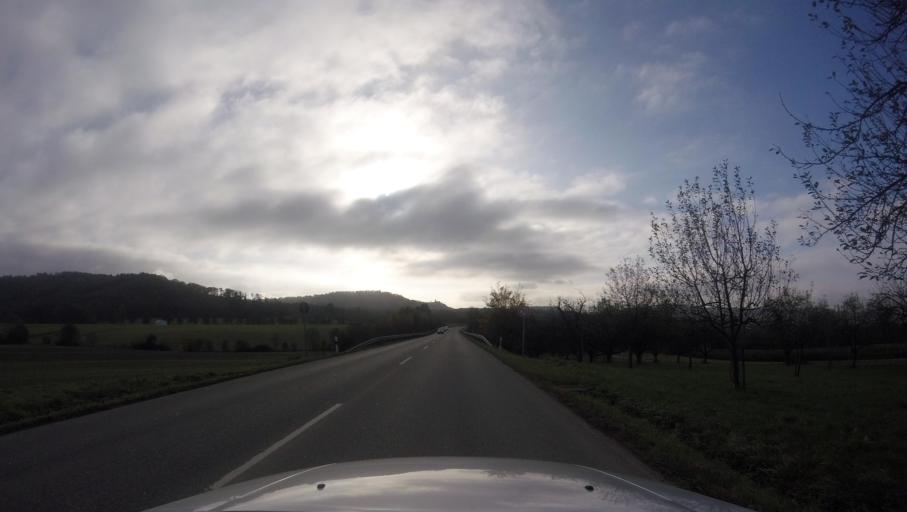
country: DE
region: Baden-Wuerttemberg
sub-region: Regierungsbezirk Stuttgart
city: Leutenbach
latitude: 48.8982
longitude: 9.4228
